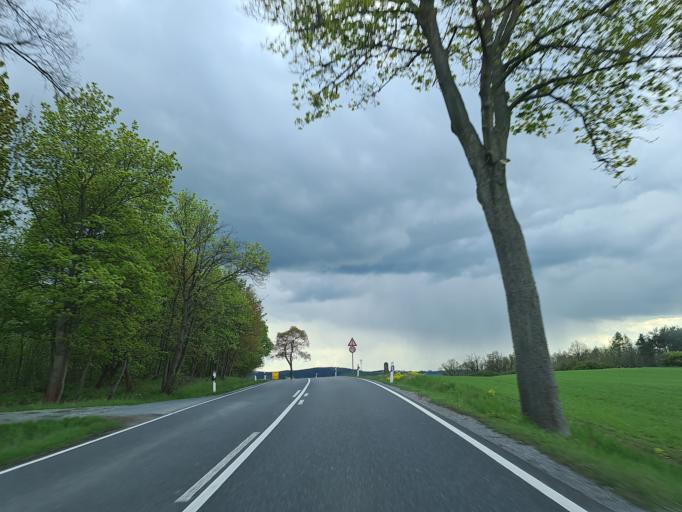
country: DE
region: Saxony
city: Weischlitz
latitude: 50.4417
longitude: 12.0942
